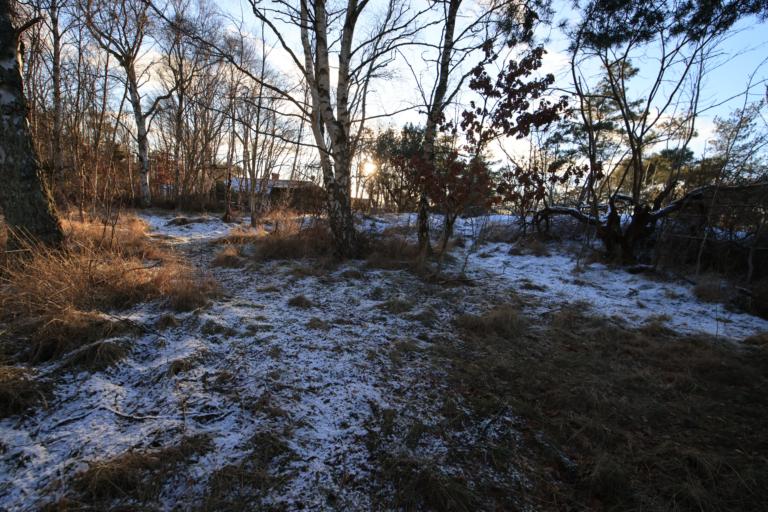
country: SE
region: Halland
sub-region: Varbergs Kommun
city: Traslovslage
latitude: 57.0644
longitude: 12.2841
